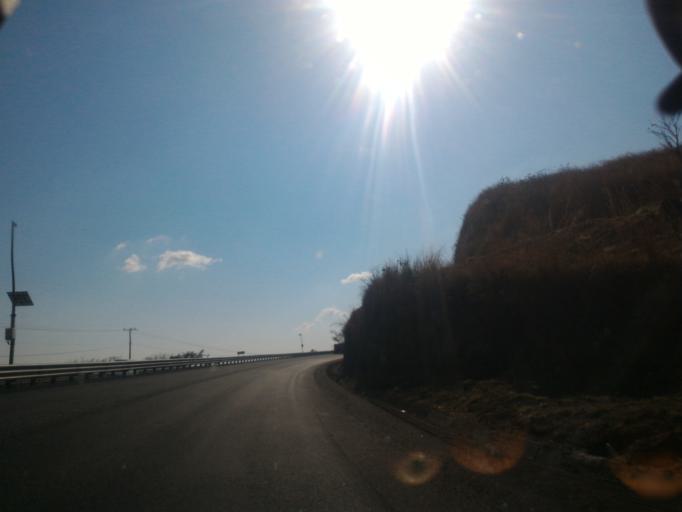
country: MX
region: Jalisco
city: Tonila
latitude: 19.4279
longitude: -103.4987
